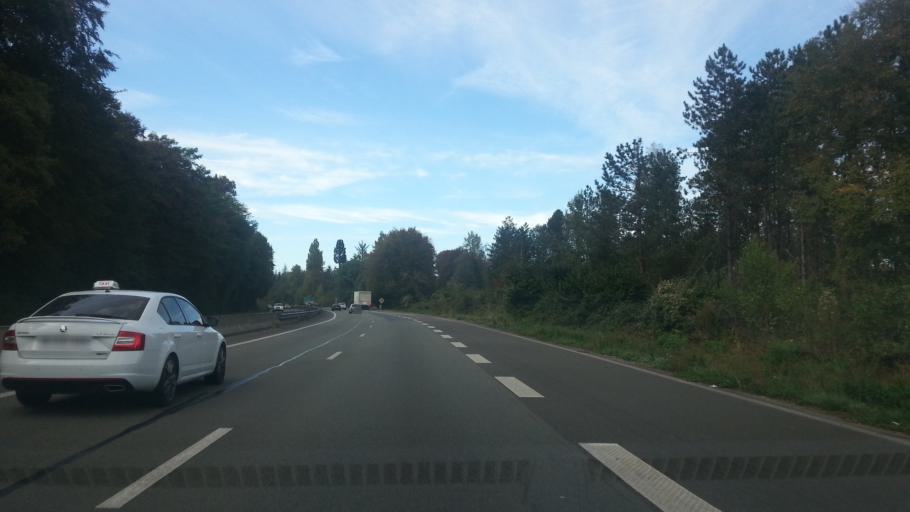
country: FR
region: Picardie
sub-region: Departement de l'Oise
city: Avilly-Saint-Leonard
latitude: 49.2334
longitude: 2.5364
